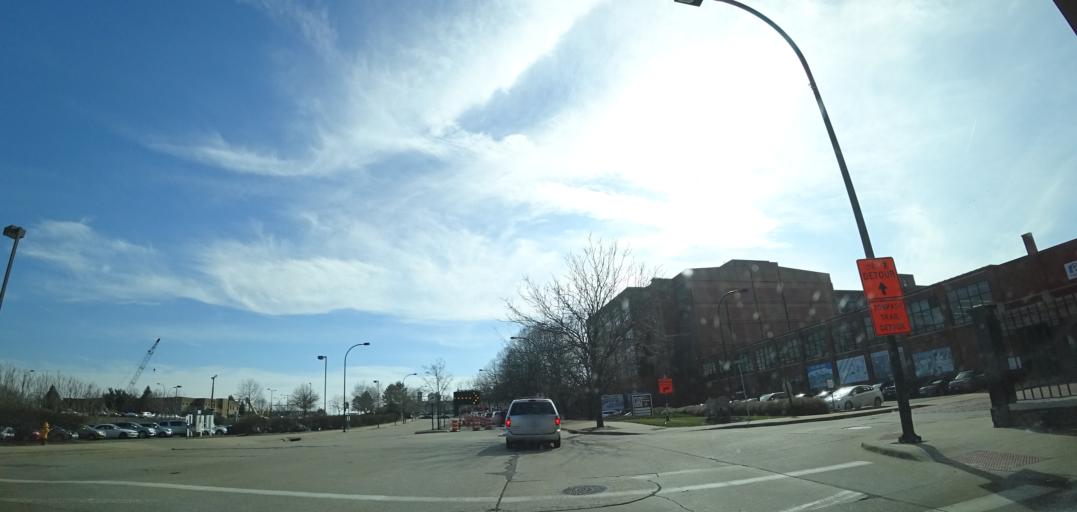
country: US
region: Ohio
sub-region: Summit County
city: Akron
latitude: 41.0708
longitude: -81.5262
